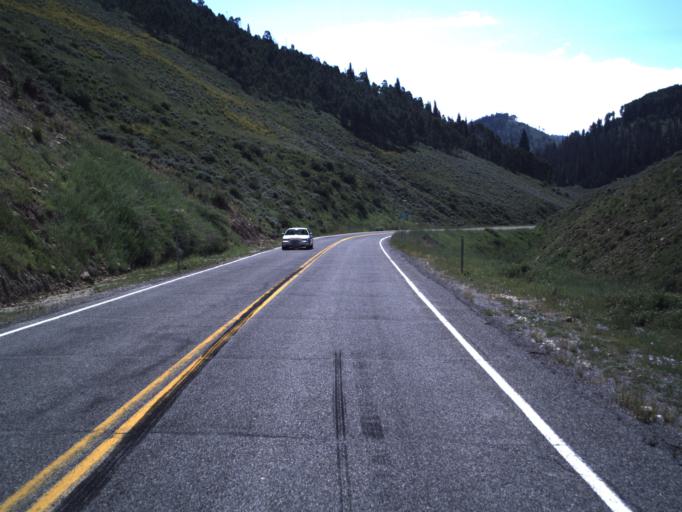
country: US
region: Utah
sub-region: Sanpete County
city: Fairview
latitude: 39.6467
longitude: -111.2489
